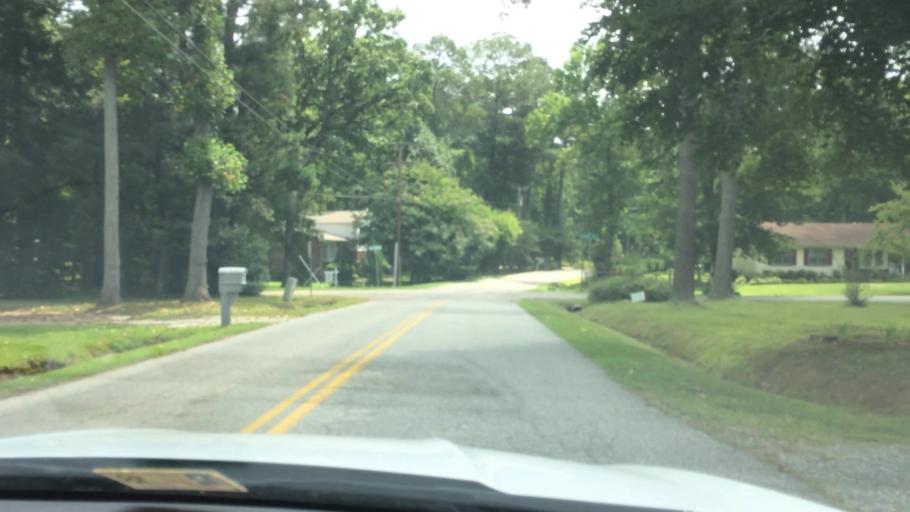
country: US
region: Virginia
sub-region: City of Poquoson
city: Poquoson
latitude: 37.1423
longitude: -76.4446
